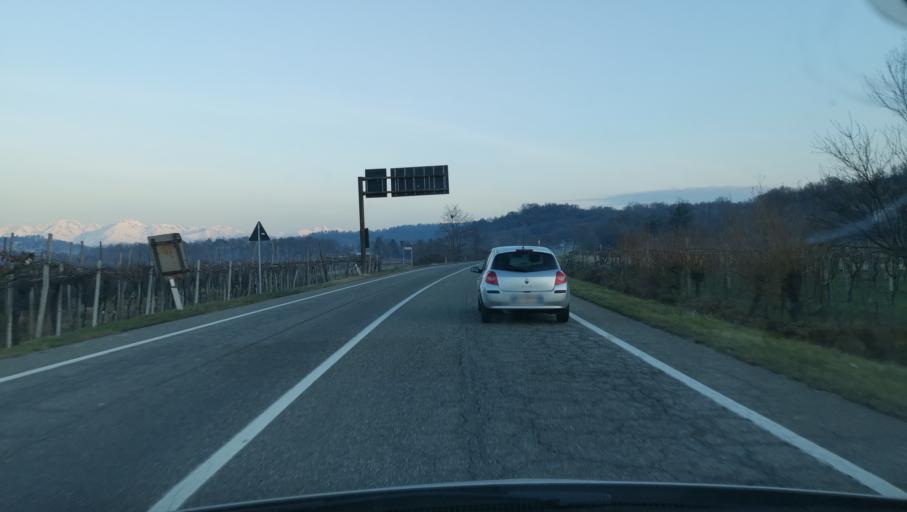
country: IT
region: Piedmont
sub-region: Provincia di Torino
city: Caluso
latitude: 45.3097
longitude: 7.8788
